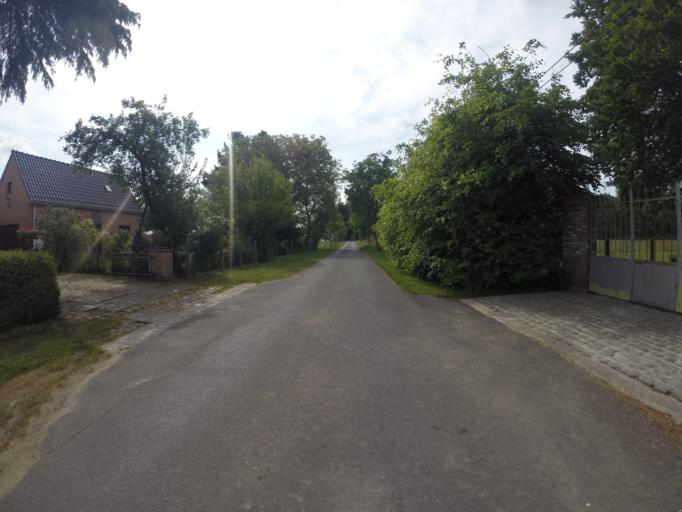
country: BE
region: Flanders
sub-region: Provincie West-Vlaanderen
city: Beernem
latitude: 51.0786
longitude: 3.3445
